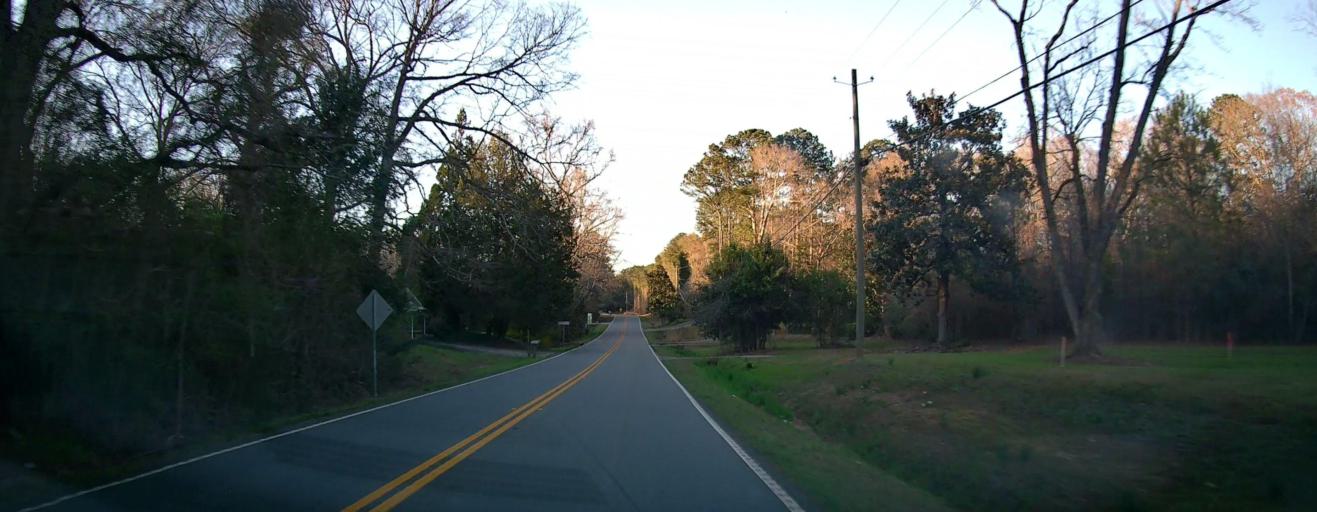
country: US
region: Georgia
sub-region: Harris County
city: Hamilton
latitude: 32.6584
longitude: -84.8672
